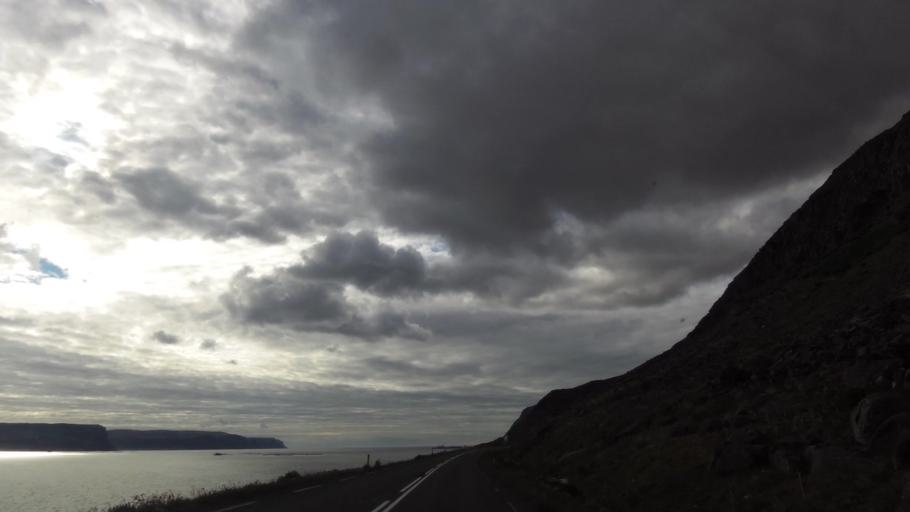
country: IS
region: West
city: Olafsvik
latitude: 65.5715
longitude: -23.9354
